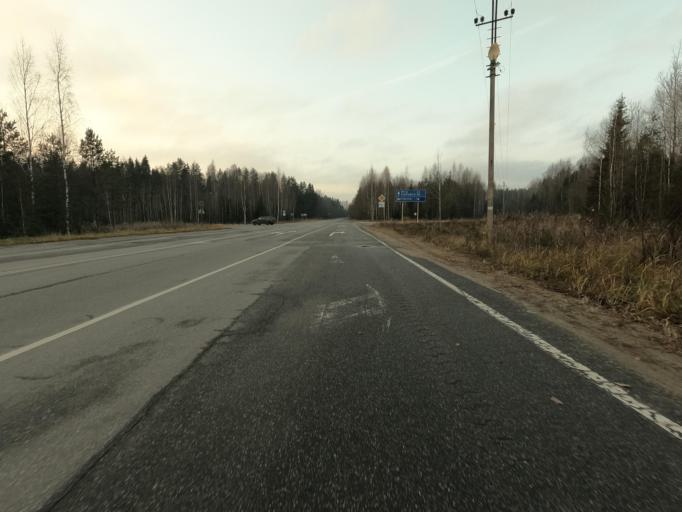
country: RU
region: Leningrad
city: Kirovsk
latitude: 59.8246
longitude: 30.9812
